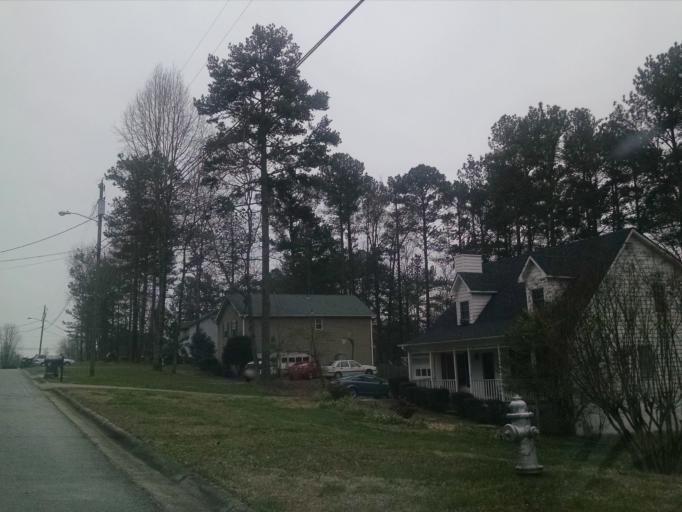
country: US
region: Georgia
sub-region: Gwinnett County
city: Sugar Hill
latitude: 34.1032
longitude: -84.0587
